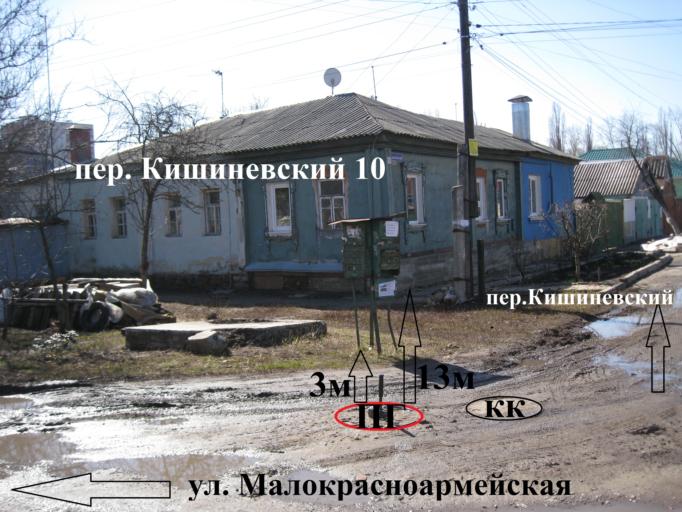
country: RU
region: Voronezj
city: Voronezh
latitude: 51.6442
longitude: 39.1831
